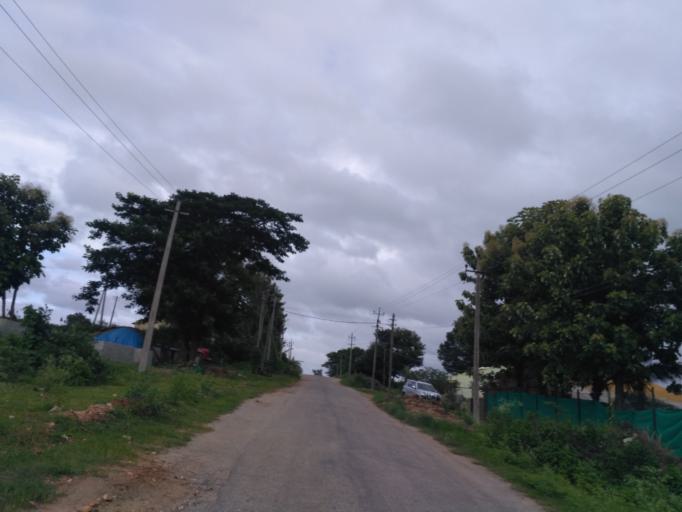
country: IN
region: Karnataka
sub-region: Hassan
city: Gorur
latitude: 12.8360
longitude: 76.1017
